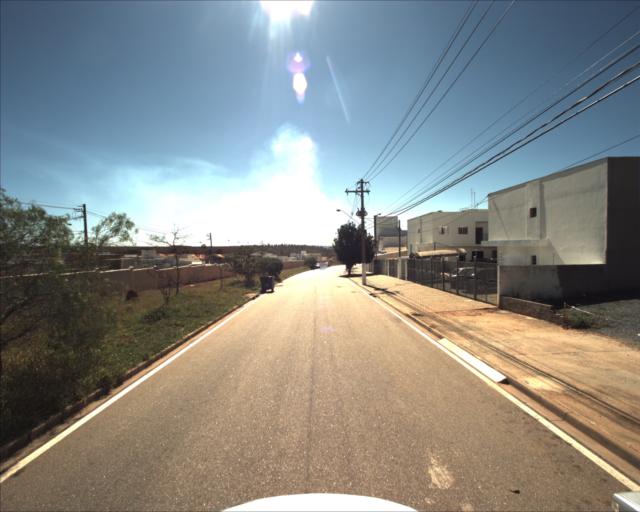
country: BR
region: Sao Paulo
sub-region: Sorocaba
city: Sorocaba
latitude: -23.4783
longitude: -47.5128
